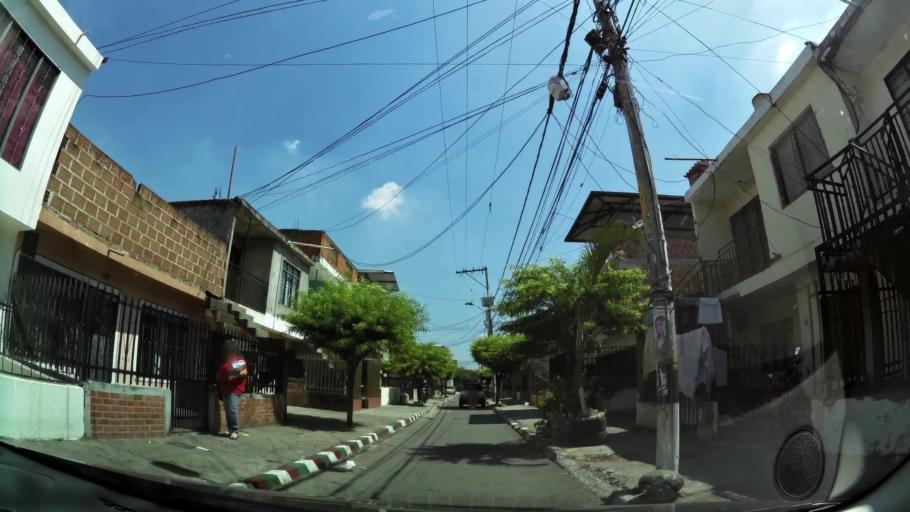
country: CO
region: Valle del Cauca
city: Cali
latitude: 3.4282
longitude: -76.5015
